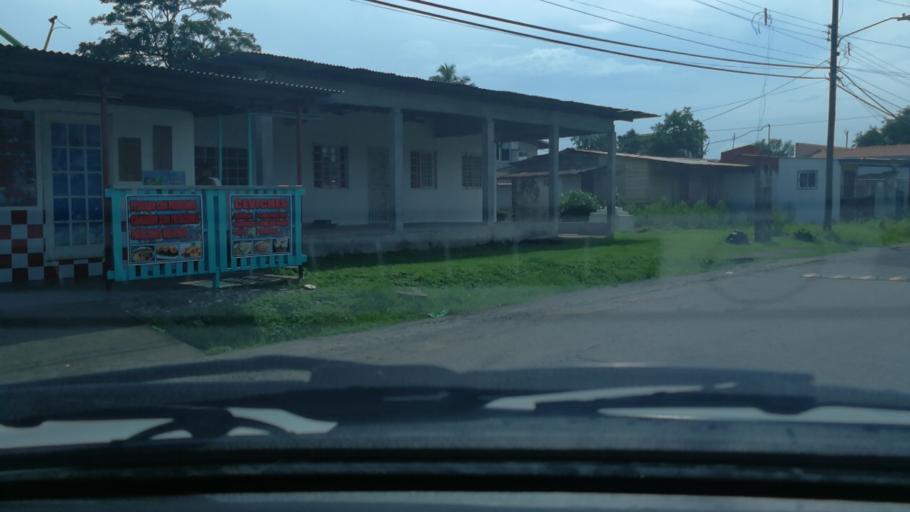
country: PA
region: Panama
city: Pacora
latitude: 9.0824
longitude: -79.2883
